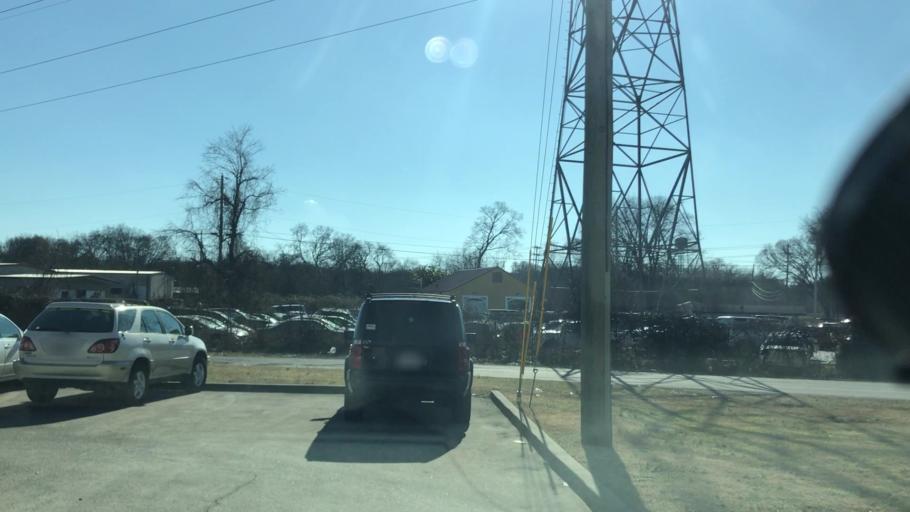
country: US
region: Tennessee
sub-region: Rutherford County
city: La Vergne
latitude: 36.0197
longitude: -86.5778
